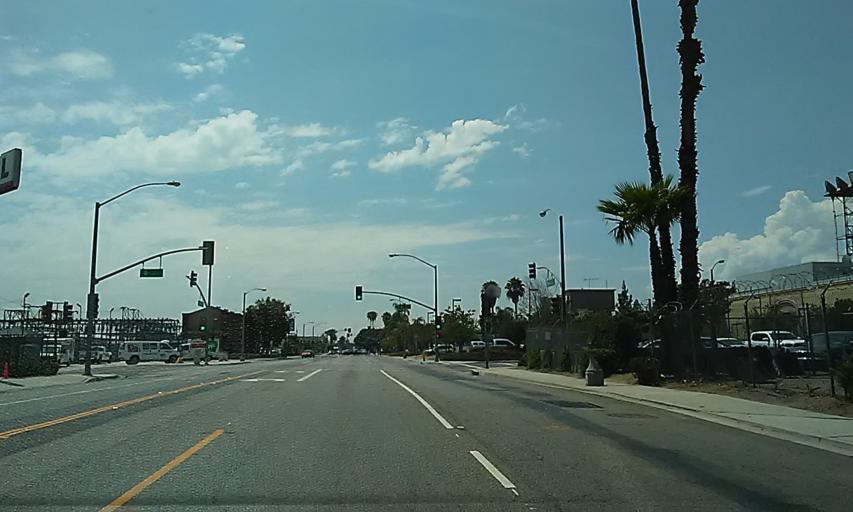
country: US
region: California
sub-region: San Bernardino County
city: San Bernardino
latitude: 34.1009
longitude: -117.2911
